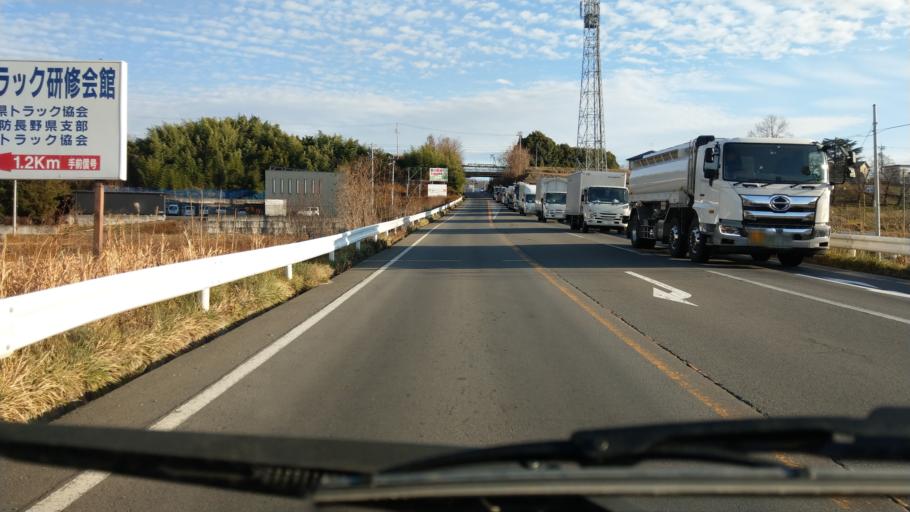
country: JP
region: Nagano
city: Ueda
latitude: 36.3950
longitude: 138.2986
